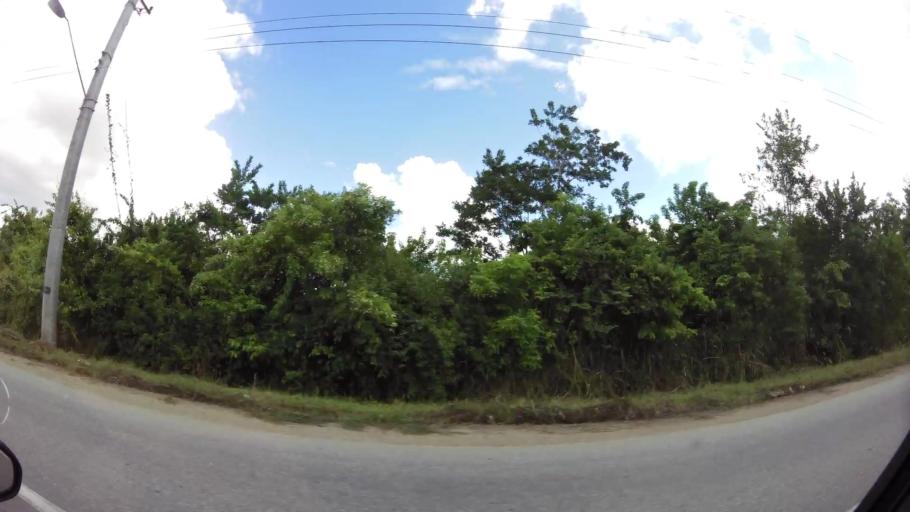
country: TT
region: Penal/Debe
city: Debe
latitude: 10.2322
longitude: -61.4329
